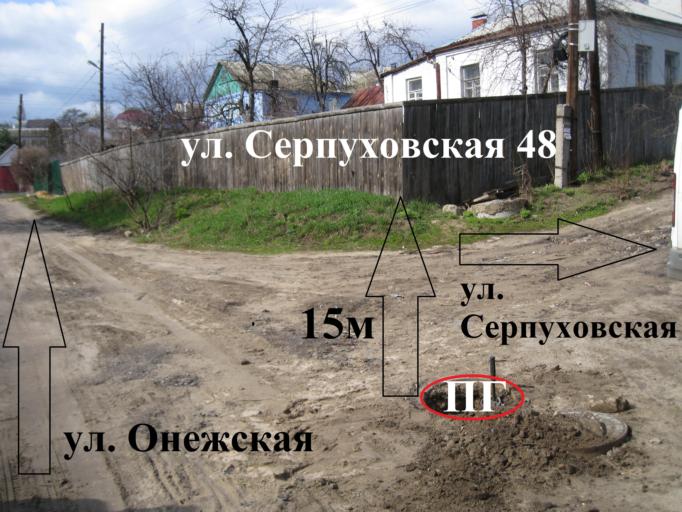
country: RU
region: Voronezj
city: Voronezh
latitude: 51.6288
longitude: 39.1859
